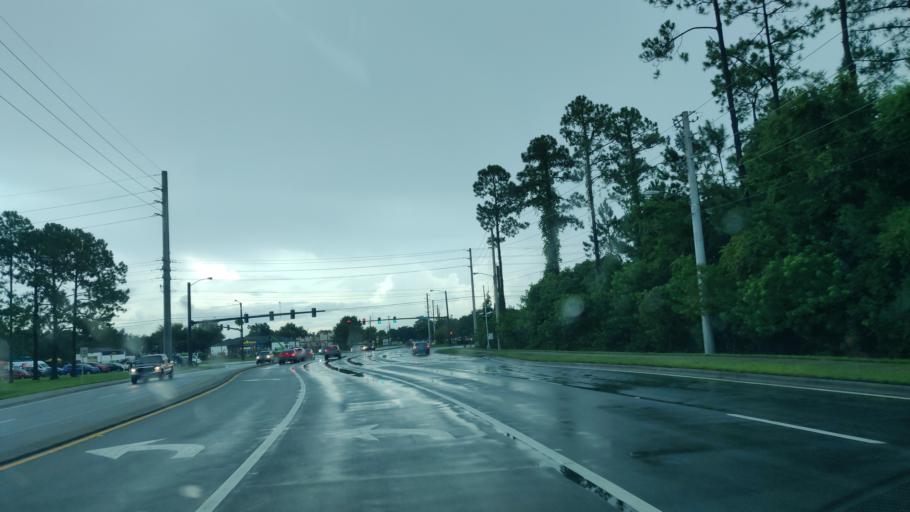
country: US
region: Florida
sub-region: Osceola County
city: Kissimmee
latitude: 28.3260
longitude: -81.4174
